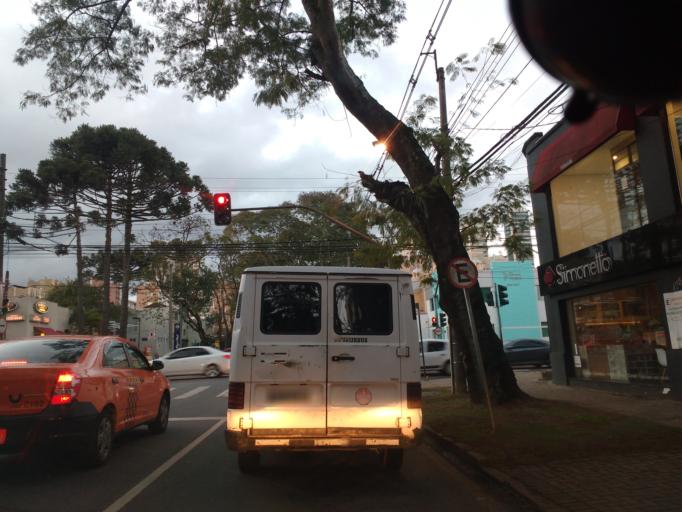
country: BR
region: Parana
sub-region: Curitiba
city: Curitiba
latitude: -25.4265
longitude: -49.2857
